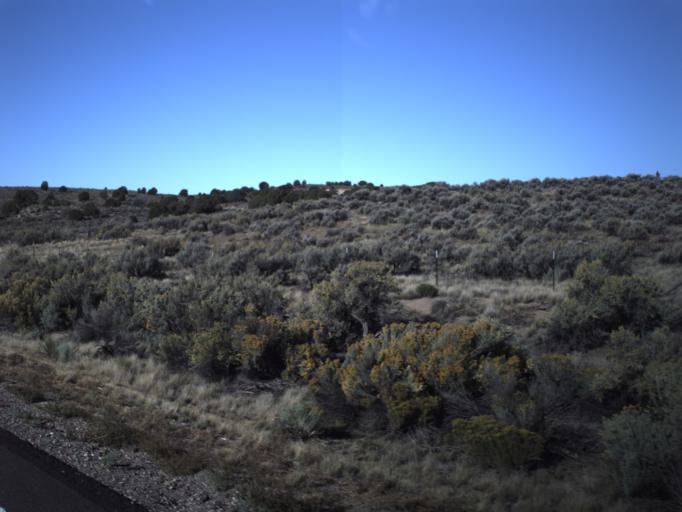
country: US
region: Utah
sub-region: Washington County
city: Enterprise
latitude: 37.7425
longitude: -114.0119
